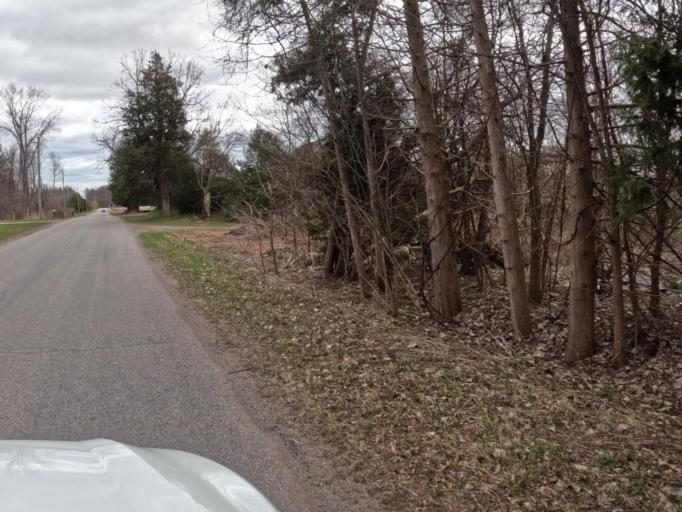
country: CA
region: Ontario
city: Norfolk County
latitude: 42.7964
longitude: -80.3622
